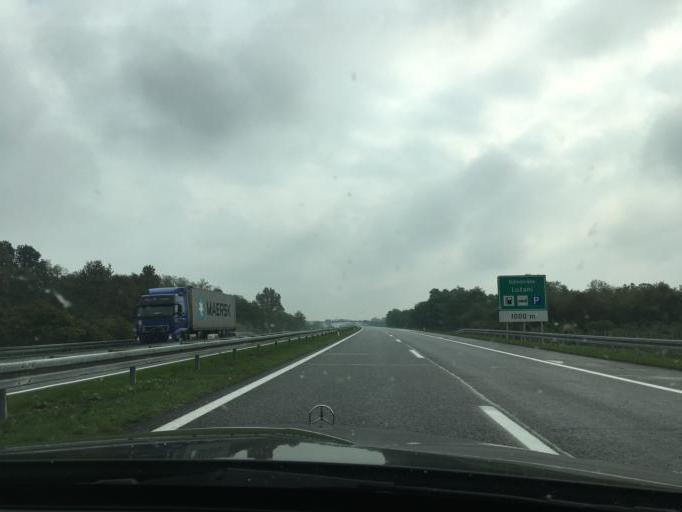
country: HR
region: Brodsko-Posavska
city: Luzani
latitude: 45.1656
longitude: 17.6829
